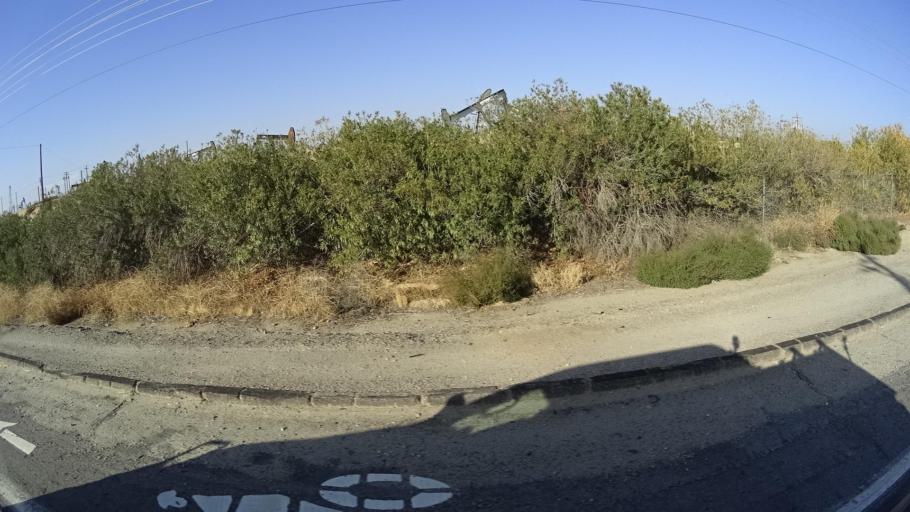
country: US
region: California
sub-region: Kern County
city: Oildale
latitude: 35.4269
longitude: -118.9994
